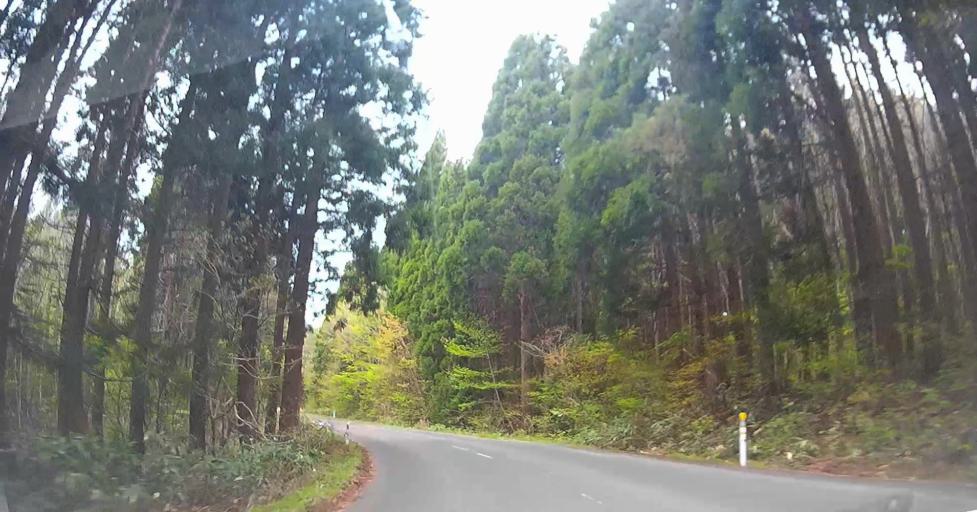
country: JP
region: Aomori
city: Goshogawara
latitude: 40.9052
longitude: 140.5119
